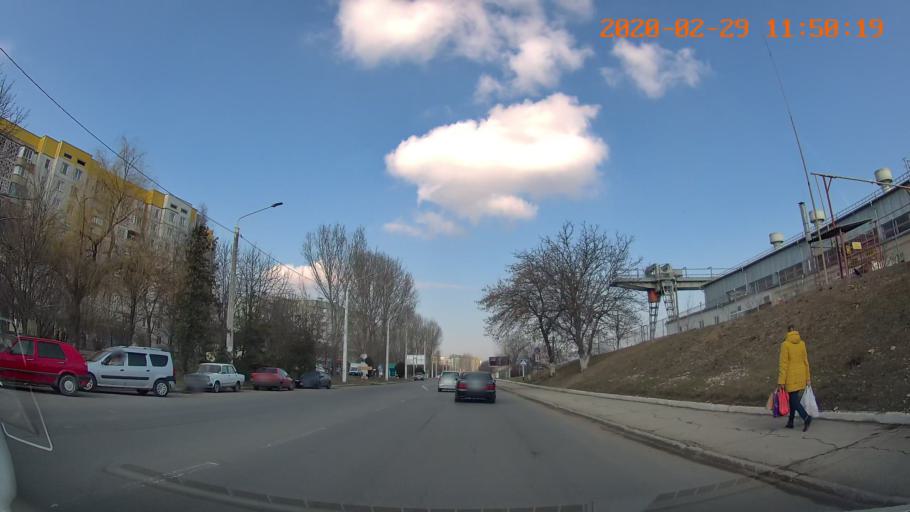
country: MD
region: Telenesti
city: Ribnita
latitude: 47.7573
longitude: 28.9910
